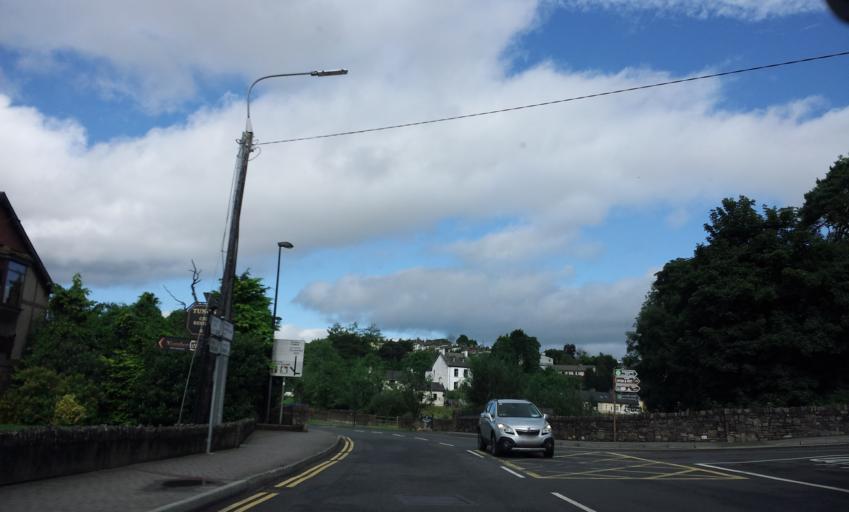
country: IE
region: Munster
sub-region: County Cork
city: Blarney
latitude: 51.9336
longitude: -8.5609
